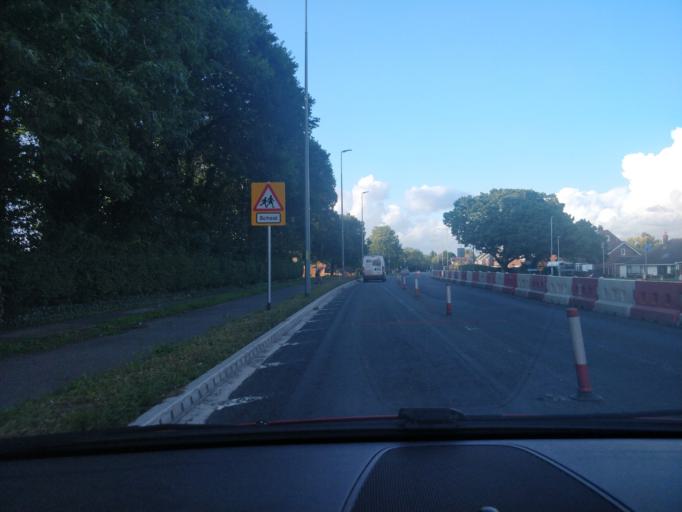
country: GB
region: England
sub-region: Lancashire
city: Preston
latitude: 53.7415
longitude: -2.7482
